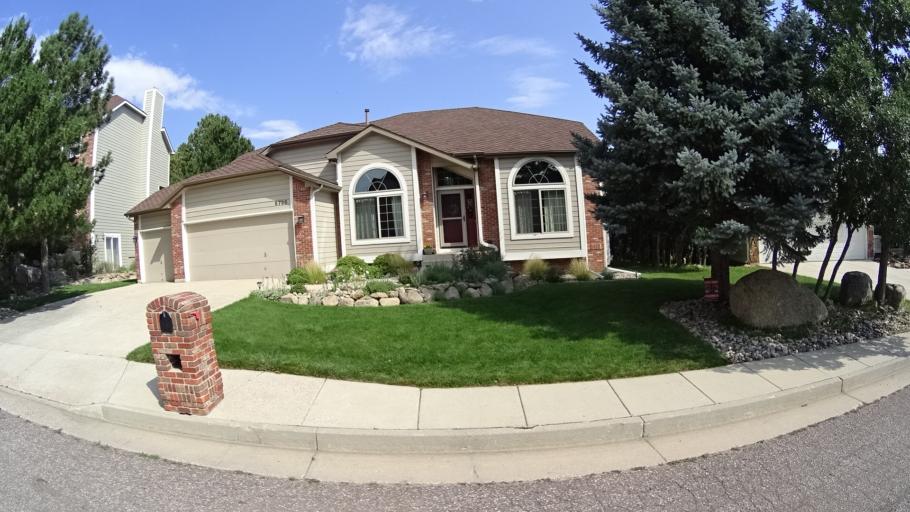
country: US
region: Colorado
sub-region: El Paso County
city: Fort Carson
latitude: 38.7477
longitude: -104.8323
